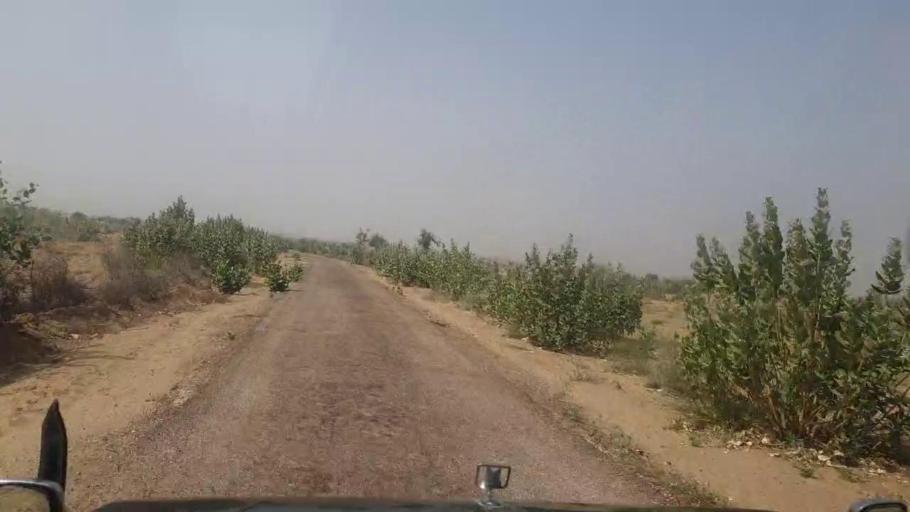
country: PK
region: Sindh
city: Islamkot
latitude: 25.0940
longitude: 70.1699
